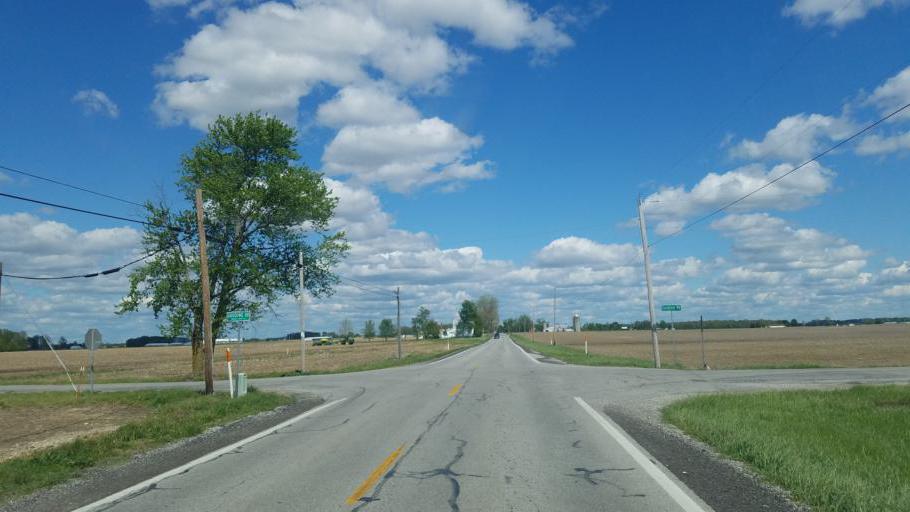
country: US
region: Ohio
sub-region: Marion County
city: Prospect
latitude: 40.4517
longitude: -83.1572
